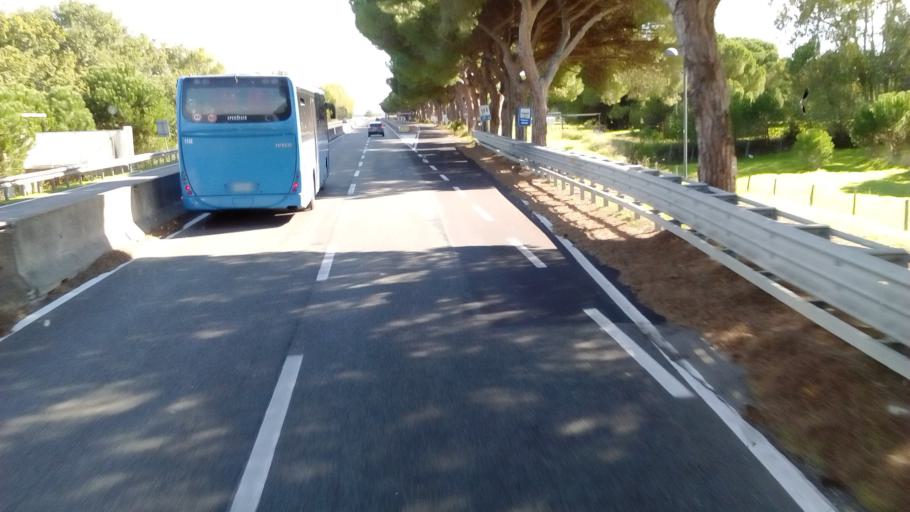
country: IT
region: Tuscany
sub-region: Provincia di Grosseto
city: Fonteblanda
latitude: 42.5396
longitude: 11.1815
